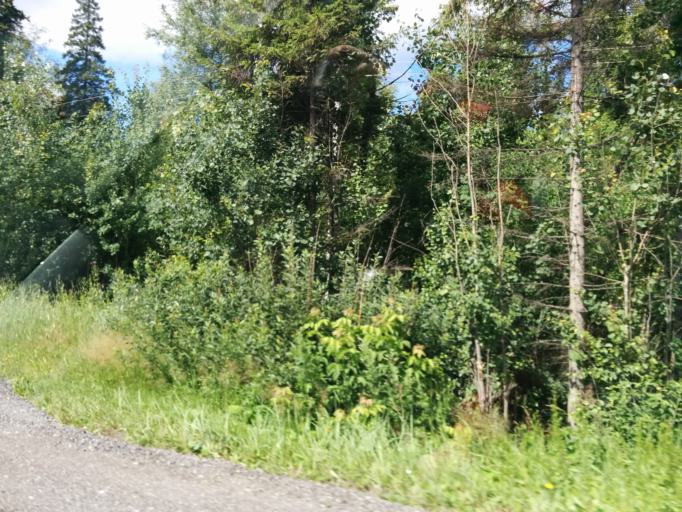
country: RU
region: Perm
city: Kondratovo
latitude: 58.0493
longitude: 56.0640
